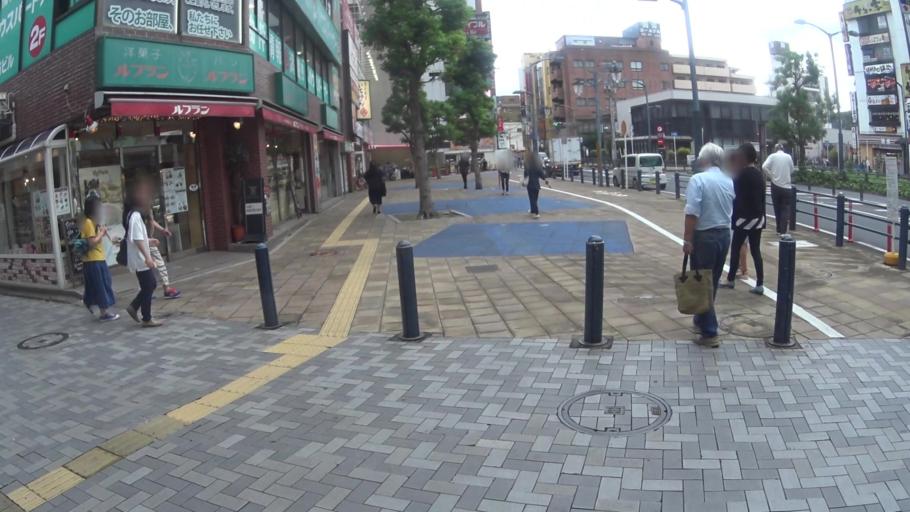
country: JP
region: Chiba
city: Nagareyama
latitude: 35.8260
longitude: 139.9204
